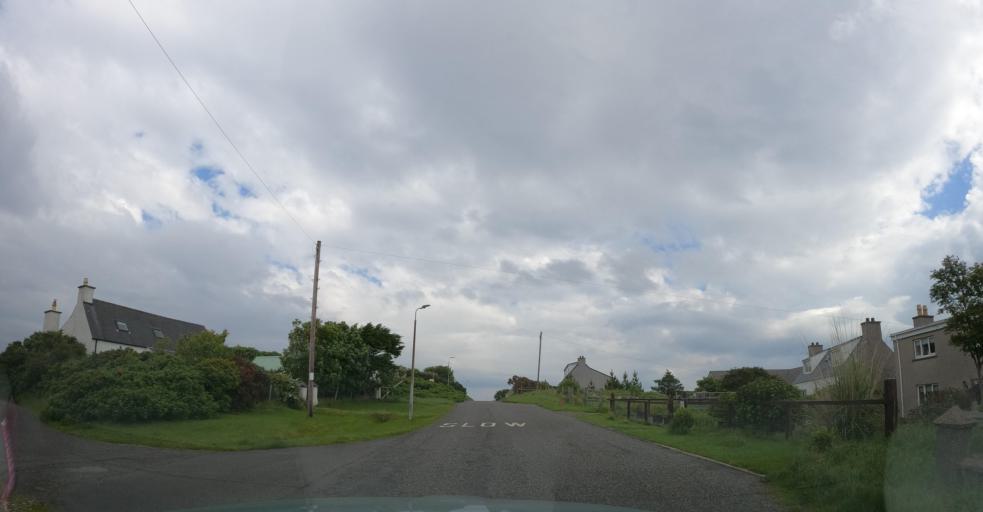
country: GB
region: Scotland
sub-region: Eilean Siar
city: Stornoway
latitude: 58.1958
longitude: -6.2233
